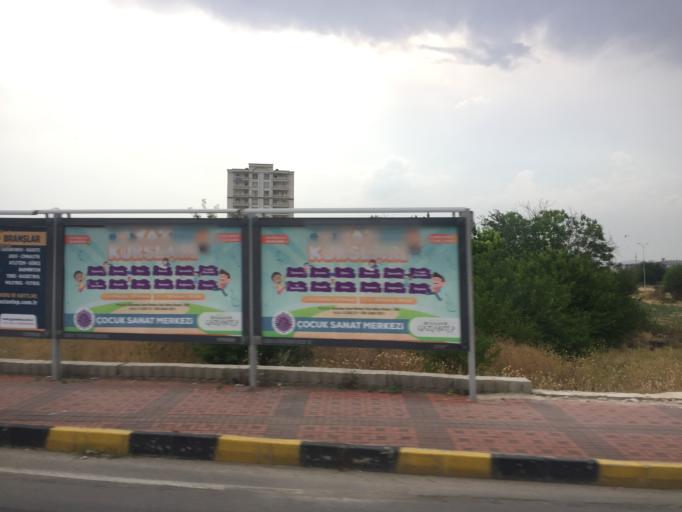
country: TR
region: Gaziantep
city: Gaziantep
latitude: 37.0562
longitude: 37.4157
